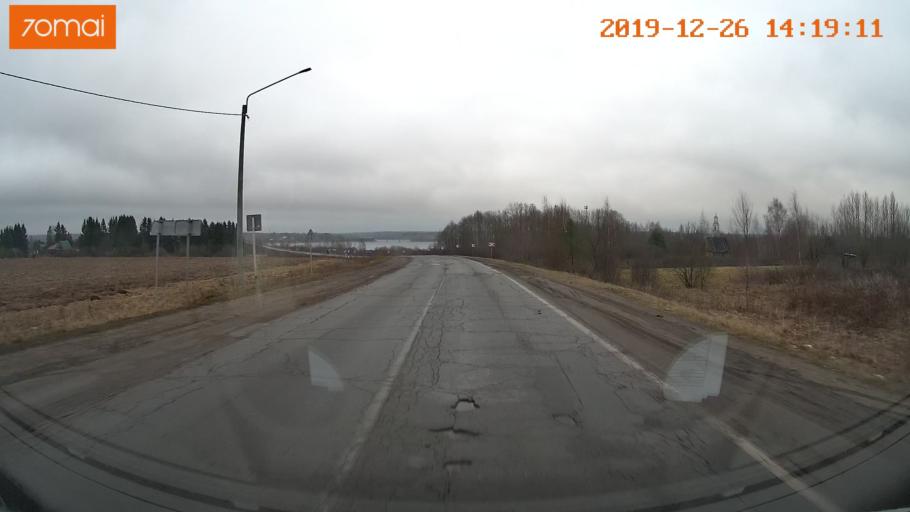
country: RU
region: Jaroslavl
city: Poshekhon'ye
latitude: 58.5113
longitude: 39.1105
